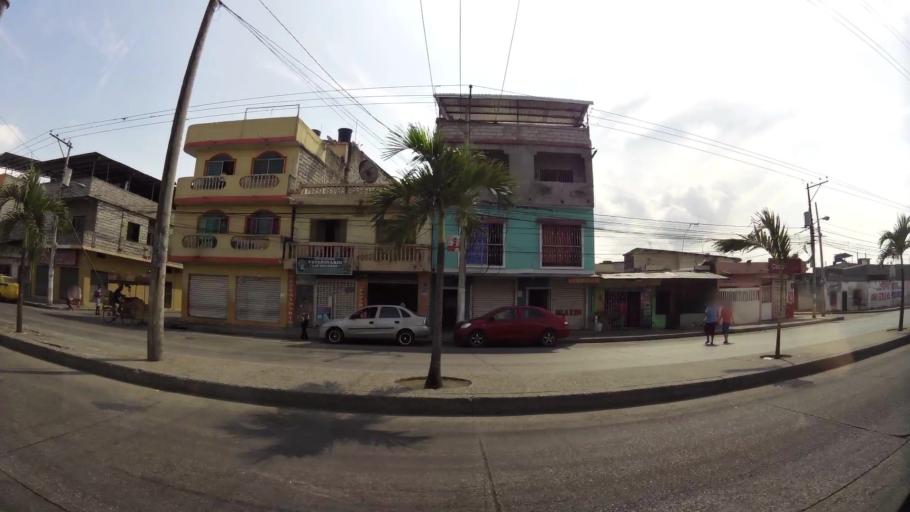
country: EC
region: Guayas
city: Guayaquil
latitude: -2.2598
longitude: -79.8839
